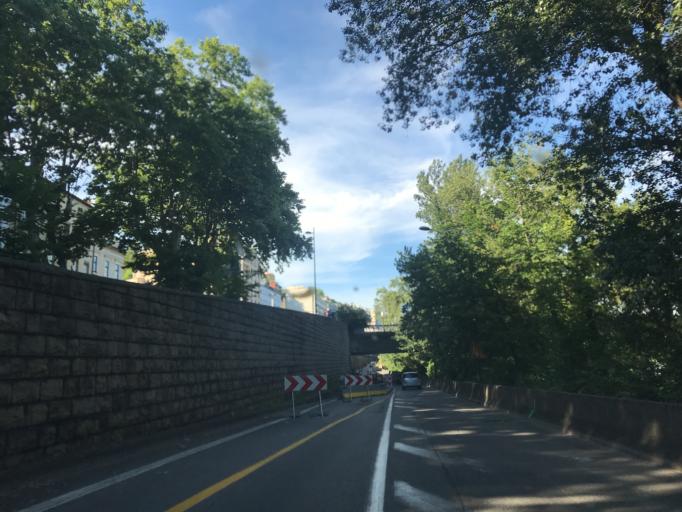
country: FR
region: Rhone-Alpes
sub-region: Departement du Rhone
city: Caluire-et-Cuire
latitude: 45.7780
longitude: 4.8409
